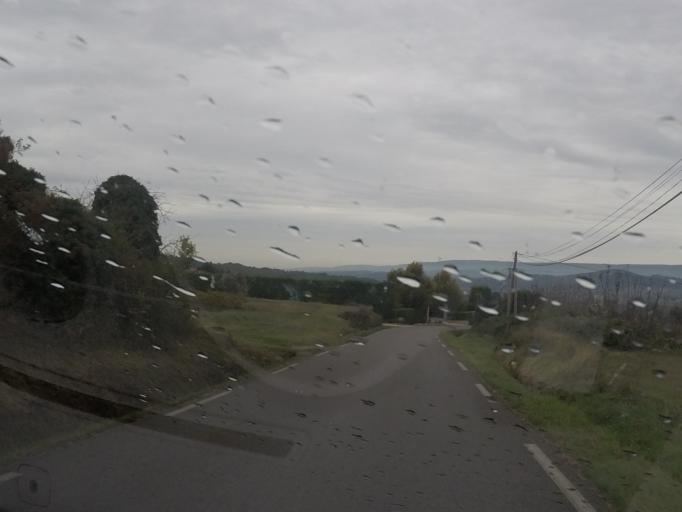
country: FR
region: Provence-Alpes-Cote d'Azur
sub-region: Departement du Vaucluse
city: Bonnieux
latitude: 43.8286
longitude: 5.2990
